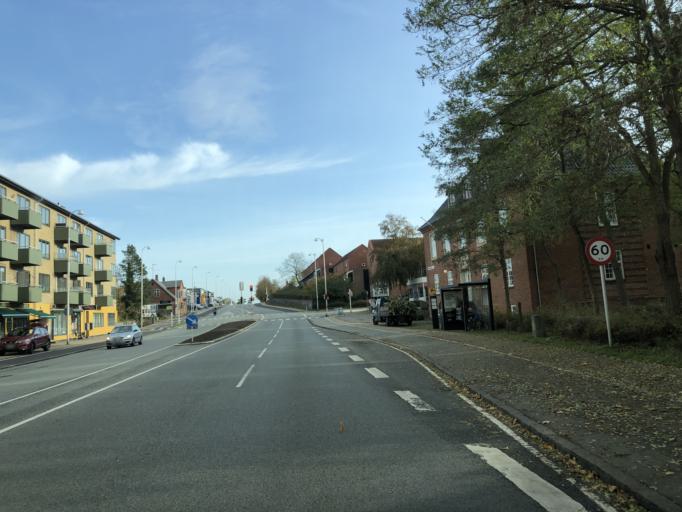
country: DK
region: Capital Region
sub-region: Rudersdal Kommune
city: Birkerod
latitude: 55.8443
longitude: 12.4338
